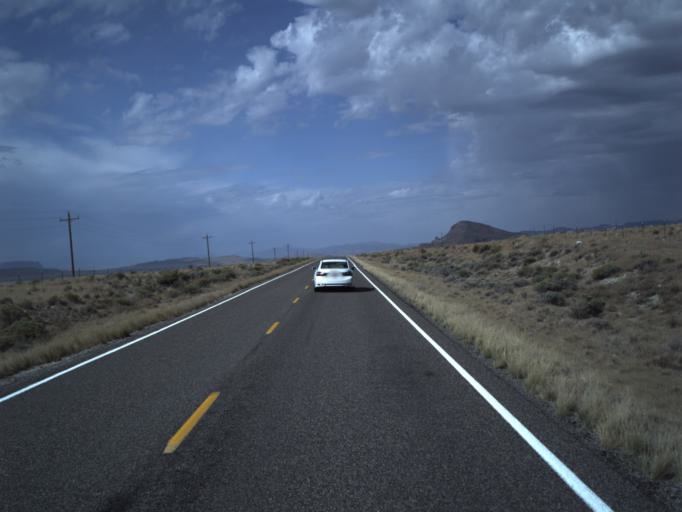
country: US
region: Utah
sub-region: Tooele County
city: Wendover
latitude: 41.4357
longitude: -113.7547
